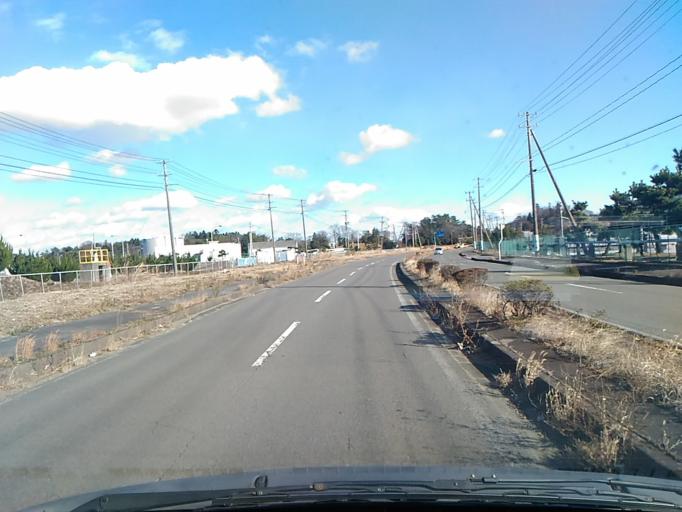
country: JP
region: Fukushima
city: Iwaki
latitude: 36.9307
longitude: 140.8582
